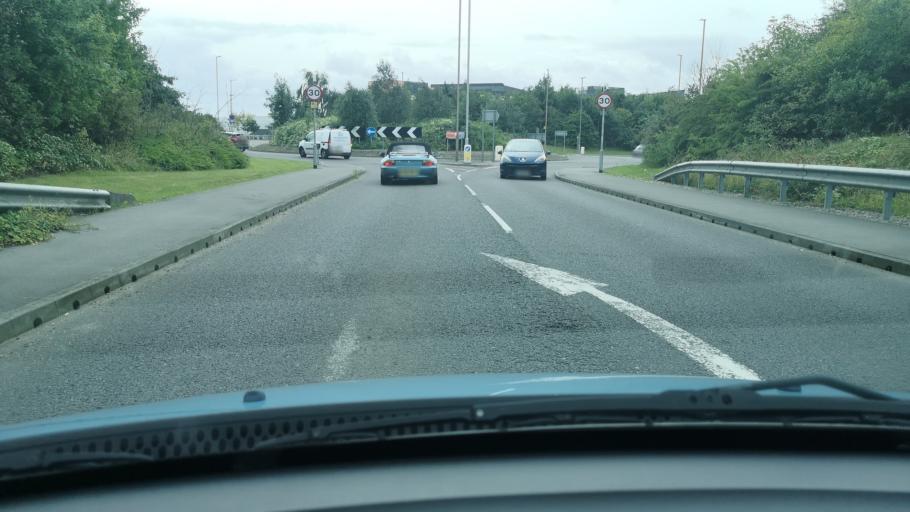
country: GB
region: England
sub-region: Barnsley
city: Shafton
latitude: 53.5883
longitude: -1.4021
